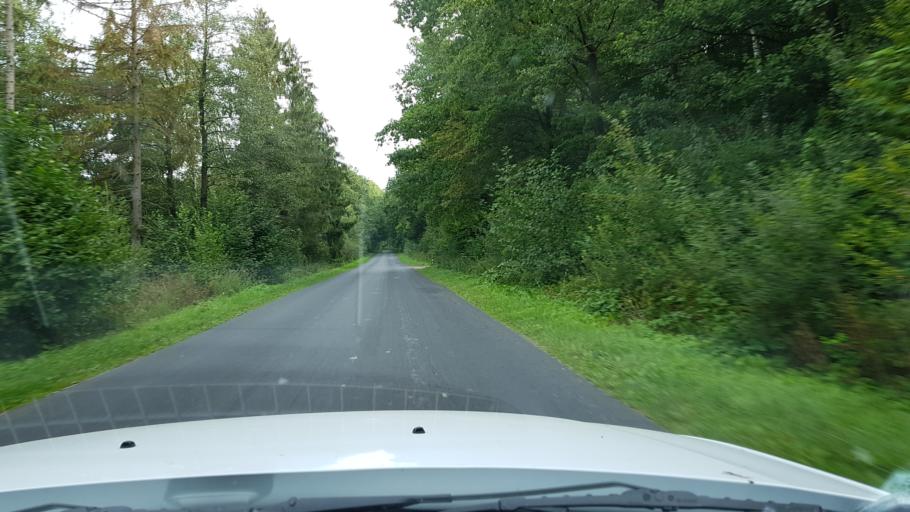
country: PL
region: West Pomeranian Voivodeship
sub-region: Powiat slawienski
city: Slawno
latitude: 54.3912
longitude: 16.6164
